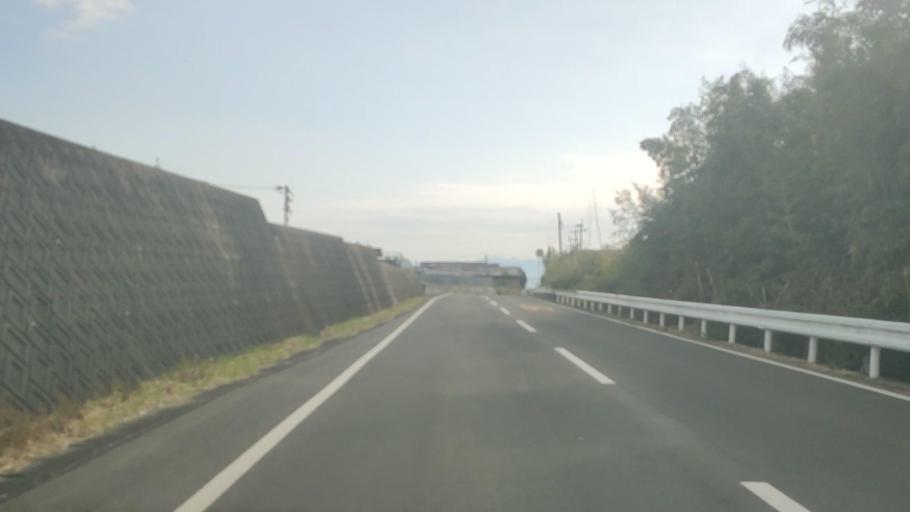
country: JP
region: Nagasaki
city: Shimabara
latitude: 32.6638
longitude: 130.2871
